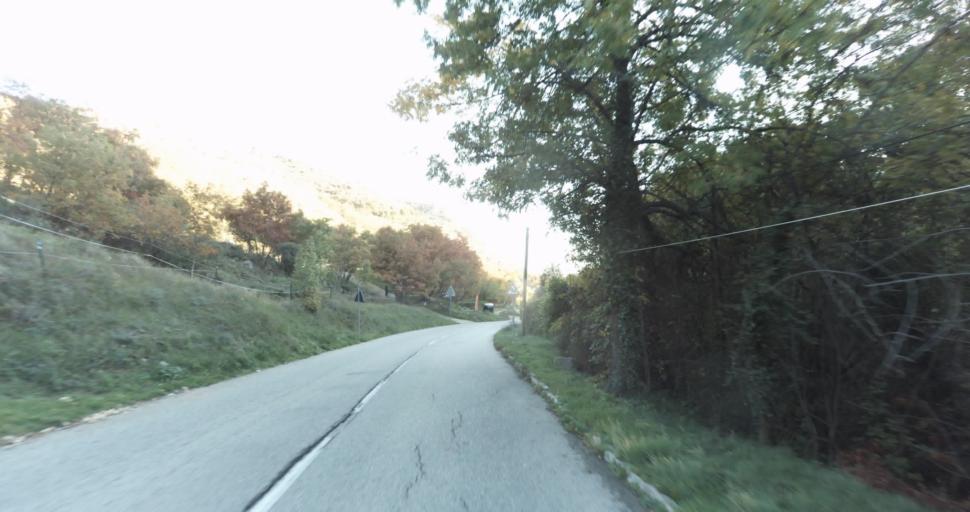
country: FR
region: Provence-Alpes-Cote d'Azur
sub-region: Departement des Alpes-Maritimes
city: Vence
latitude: 43.7412
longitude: 7.1054
